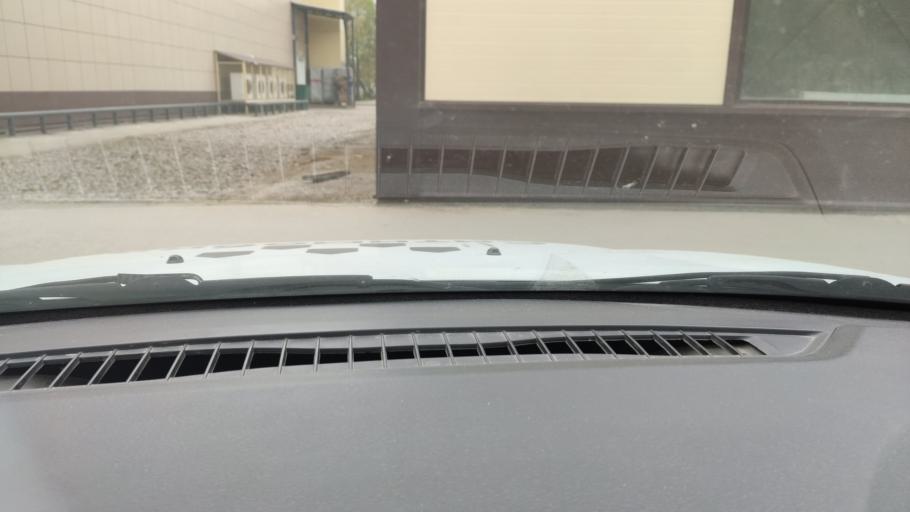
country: RU
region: Perm
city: Kungur
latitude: 57.4363
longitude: 56.9371
